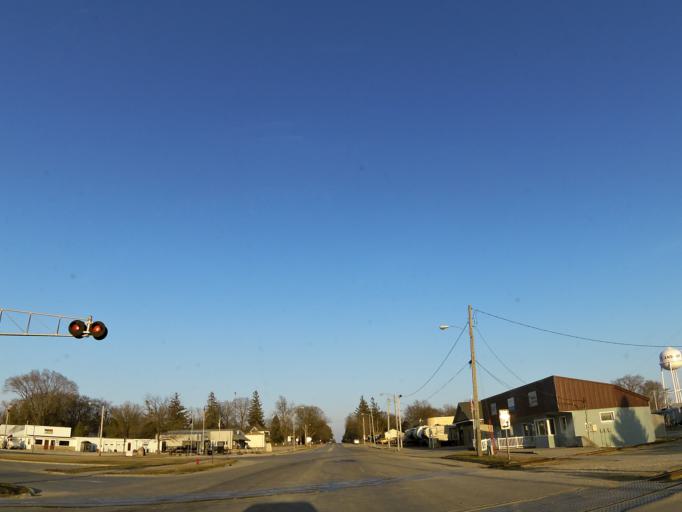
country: US
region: Iowa
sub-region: Mitchell County
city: Saint Ansgar
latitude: 43.3785
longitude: -92.9185
